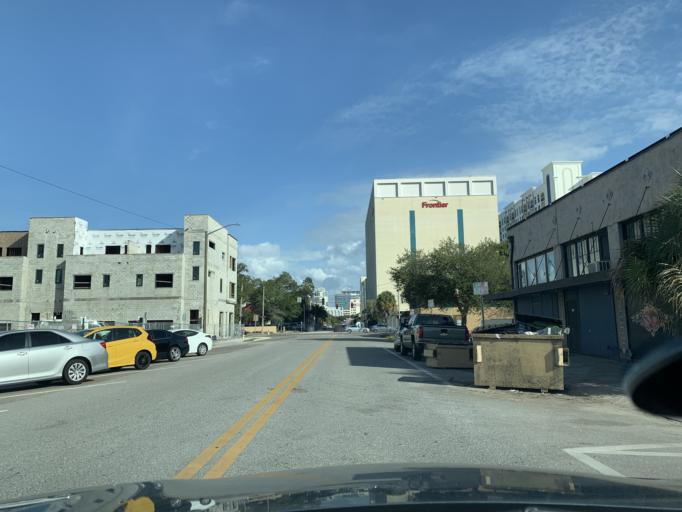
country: US
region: Florida
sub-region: Pinellas County
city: Saint Petersburg
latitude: 27.7725
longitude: -82.6476
